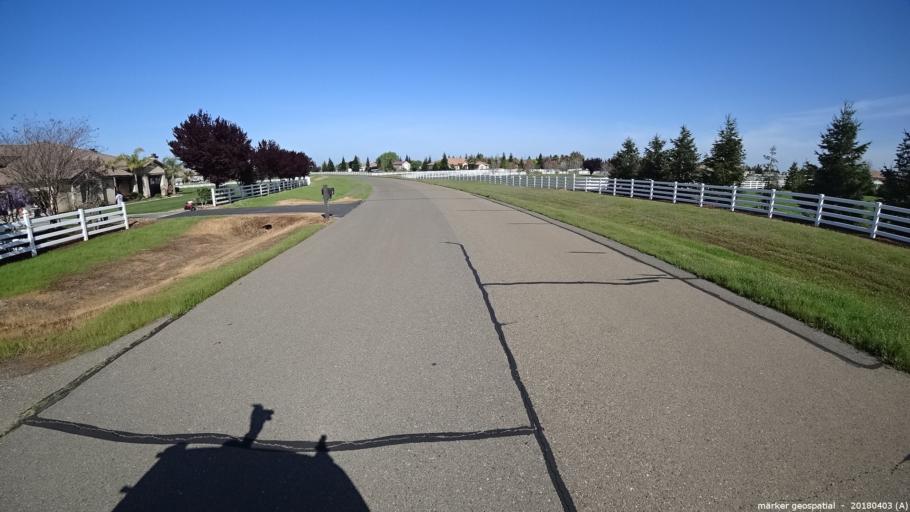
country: US
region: California
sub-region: Sacramento County
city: Clay
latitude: 38.4093
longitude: -121.1915
